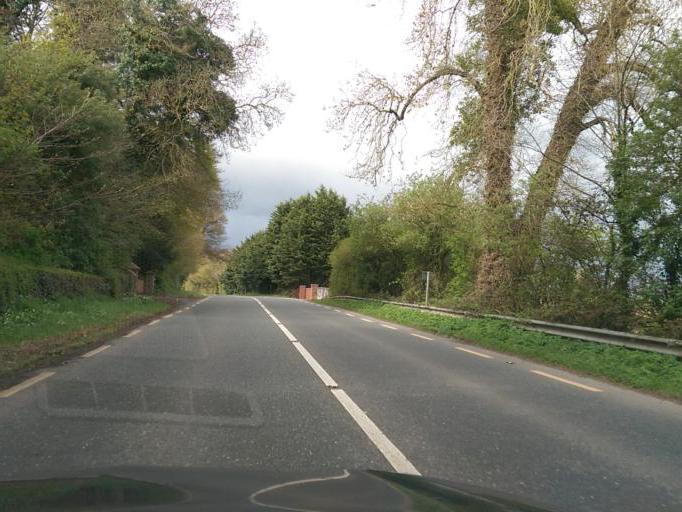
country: IE
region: Leinster
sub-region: An Mhi
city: Dunshaughlin
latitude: 53.5297
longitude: -6.5577
